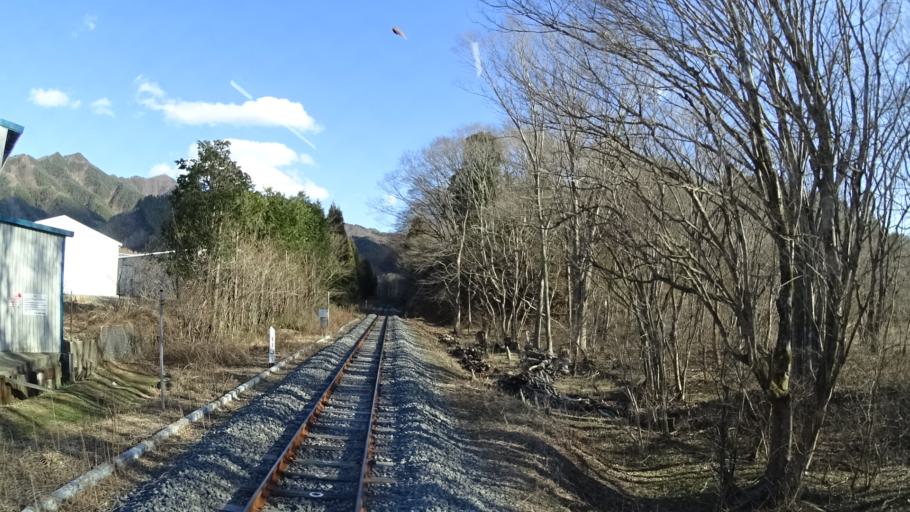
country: JP
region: Iwate
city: Miyako
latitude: 39.5582
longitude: 141.9386
